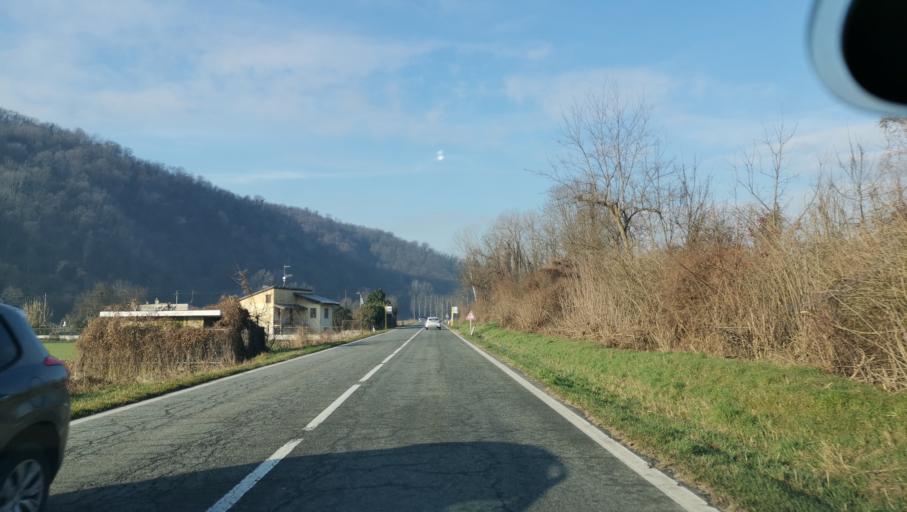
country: IT
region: Piedmont
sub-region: Provincia di Torino
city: San Sebastiano da Po
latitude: 45.1719
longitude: 7.9306
